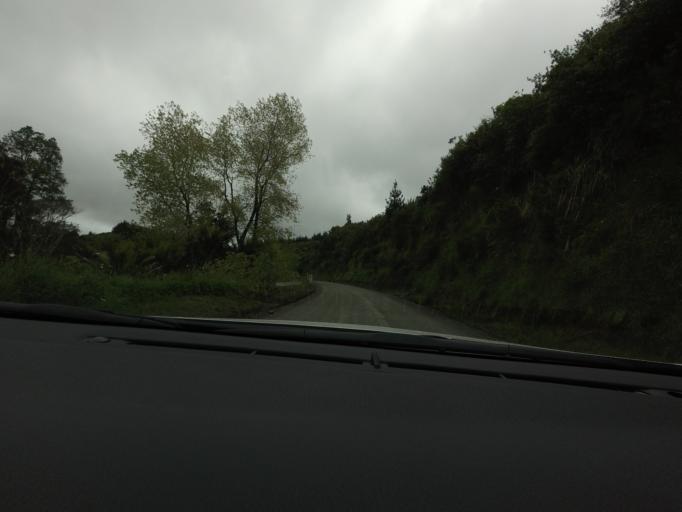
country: NZ
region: Auckland
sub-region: Auckland
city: Warkworth
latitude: -36.4846
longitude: 174.6062
